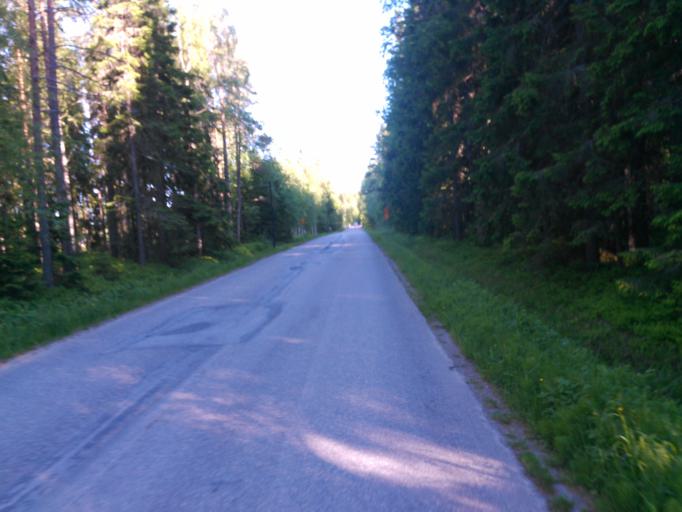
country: SE
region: Vaesterbotten
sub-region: Umea Kommun
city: Ersmark
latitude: 63.8711
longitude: 20.3317
